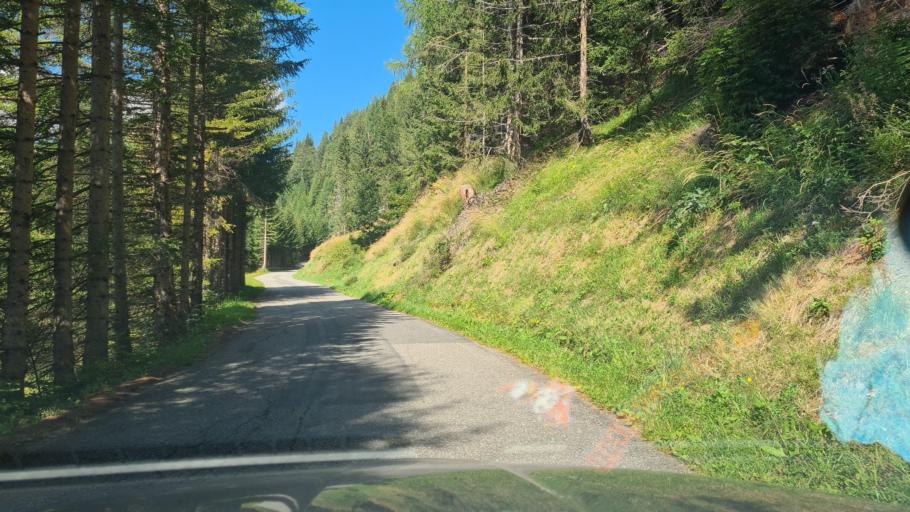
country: AT
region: Salzburg
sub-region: Politischer Bezirk Tamsweg
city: Zederhaus
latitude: 47.1848
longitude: 13.4322
